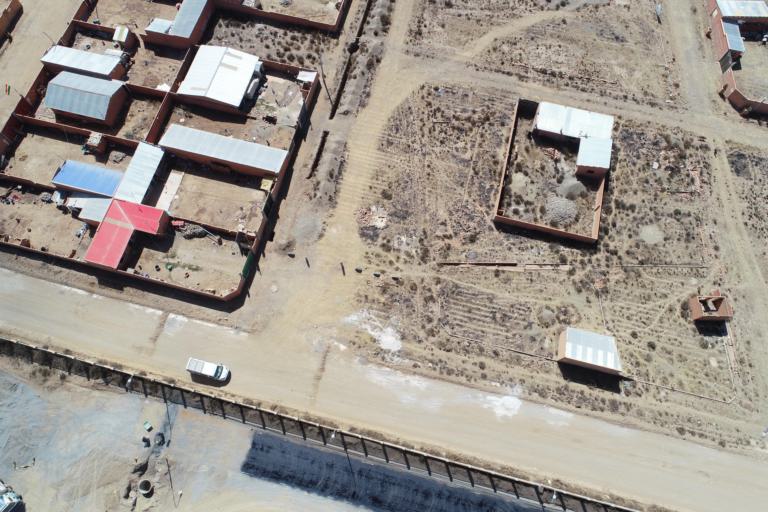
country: BO
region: La Paz
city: La Paz
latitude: -16.5961
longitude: -68.2129
